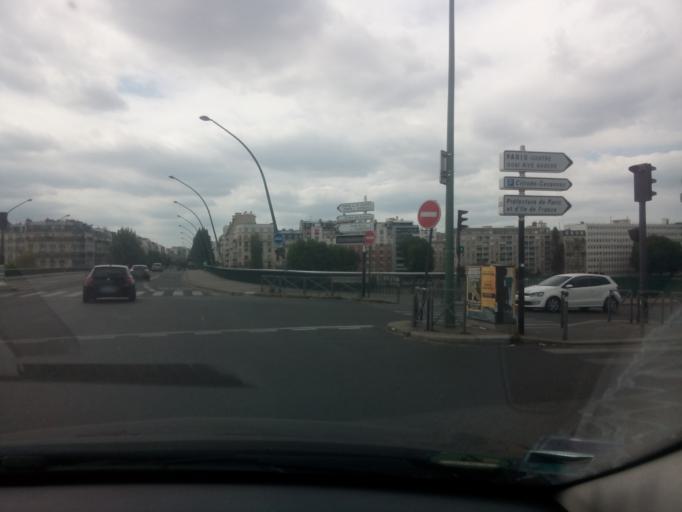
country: FR
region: Ile-de-France
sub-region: Departement des Hauts-de-Seine
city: Issy-les-Moulineaux
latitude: 48.8387
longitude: 2.2700
